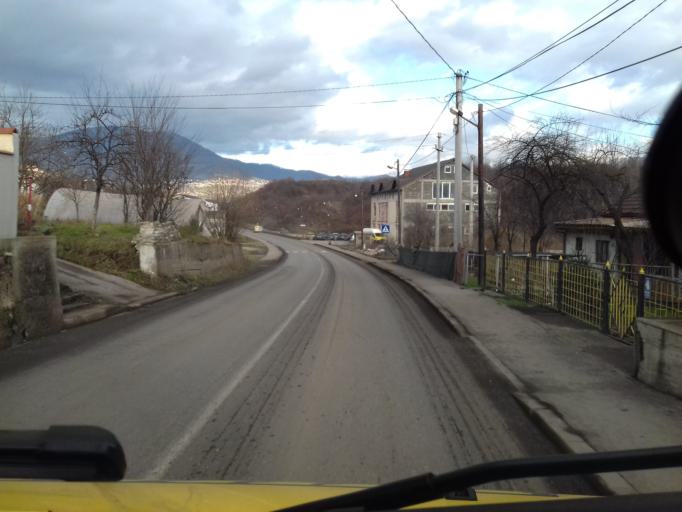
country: BA
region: Federation of Bosnia and Herzegovina
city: Zenica
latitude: 44.2072
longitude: 17.8968
